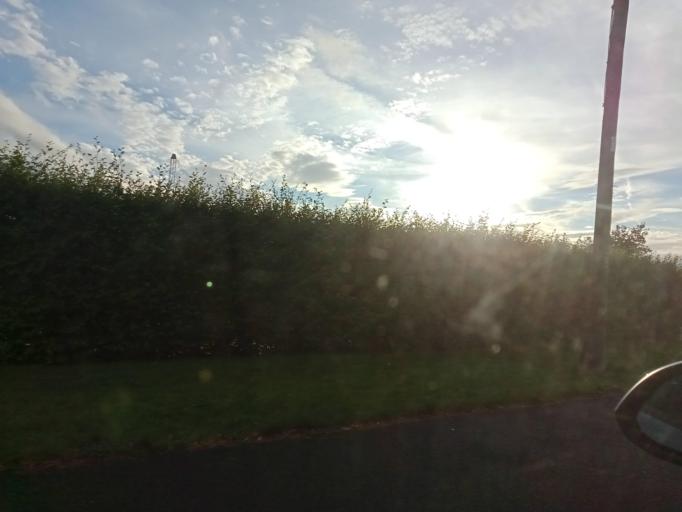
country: IE
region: Leinster
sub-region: Laois
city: Stradbally
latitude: 53.0075
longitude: -7.2172
